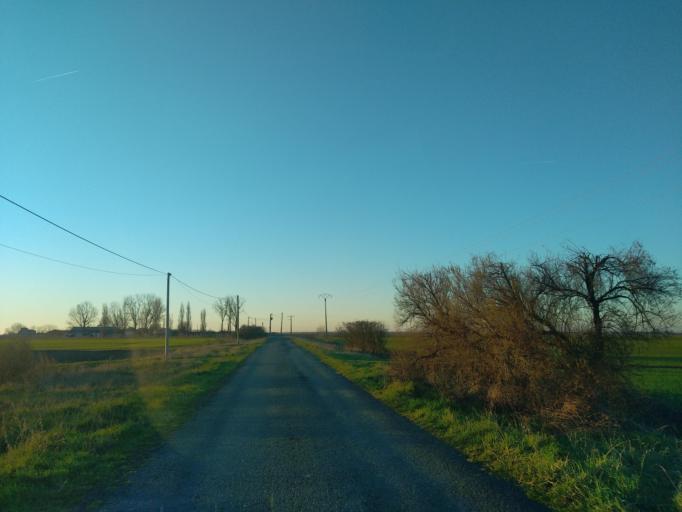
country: FR
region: Pays de la Loire
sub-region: Departement de la Vendee
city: Triaize
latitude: 46.3720
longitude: -1.2749
